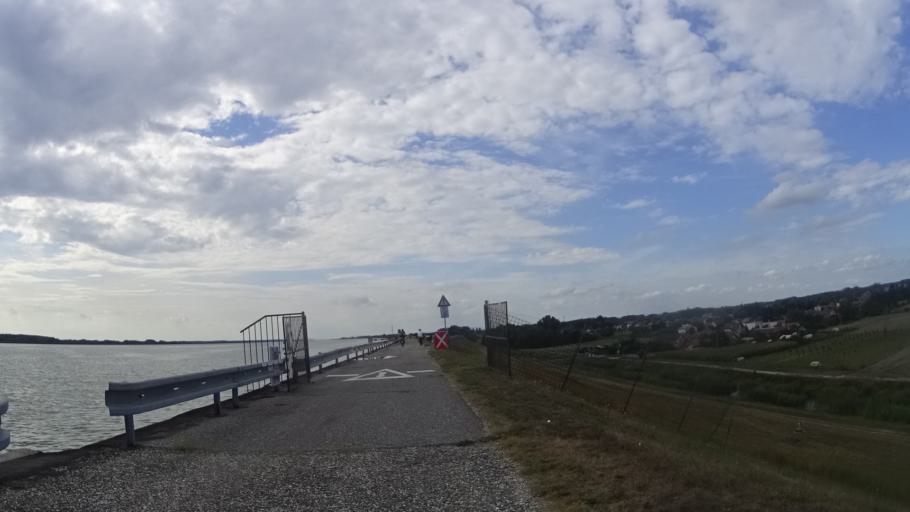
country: SK
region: Trnavsky
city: Gabcikovo
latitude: 47.8964
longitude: 17.5260
